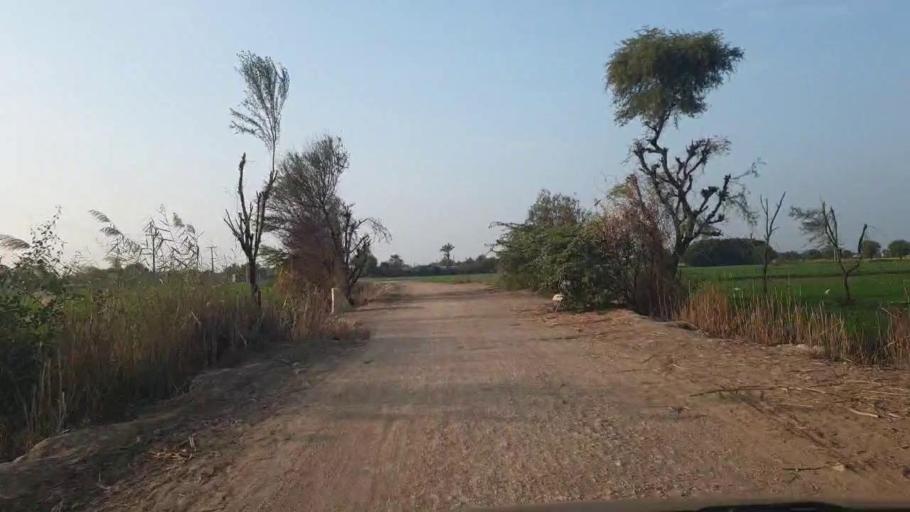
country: PK
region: Sindh
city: Berani
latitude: 25.8597
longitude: 68.7366
